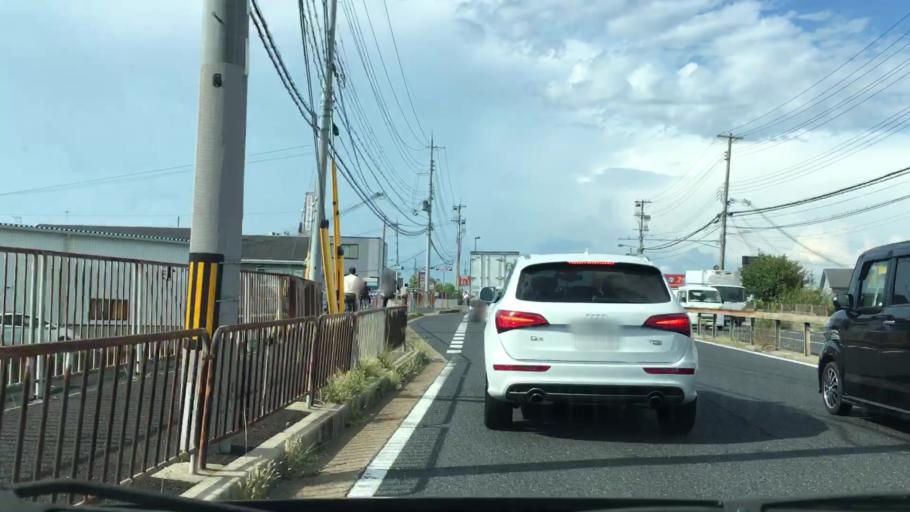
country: JP
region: Hyogo
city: Akashi
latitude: 34.6764
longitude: 134.9818
